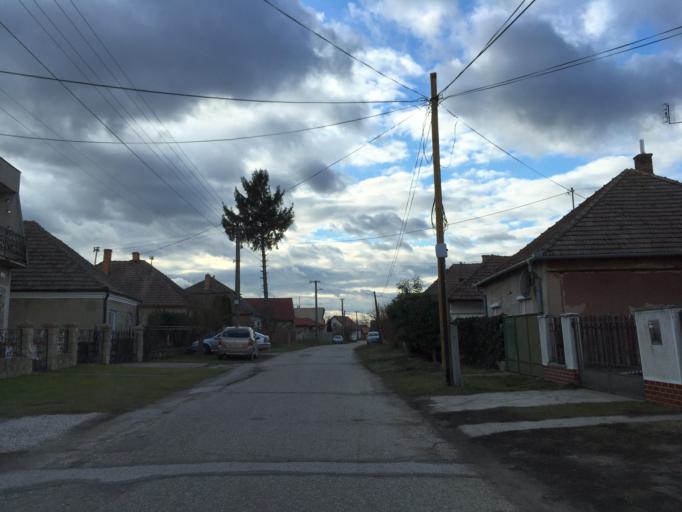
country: SK
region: Nitriansky
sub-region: Okres Nove Zamky
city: Nove Zamky
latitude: 47.9234
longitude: 18.1201
